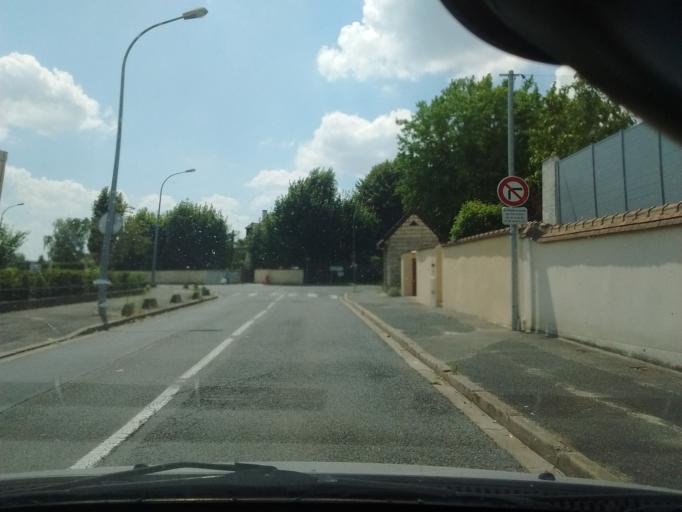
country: FR
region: Ile-de-France
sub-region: Departement de Seine-et-Marne
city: Ponthierry
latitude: 48.5322
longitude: 2.5349
